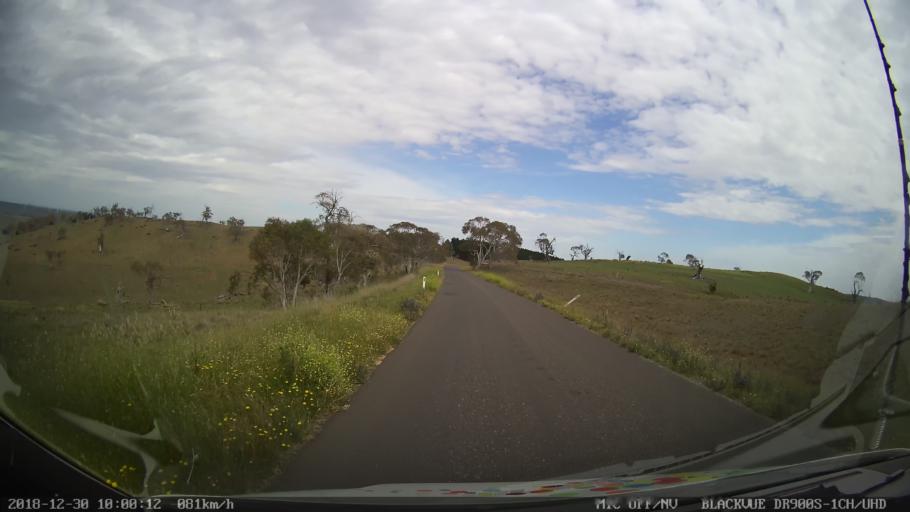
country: AU
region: New South Wales
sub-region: Cooma-Monaro
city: Cooma
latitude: -36.5179
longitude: 149.2009
